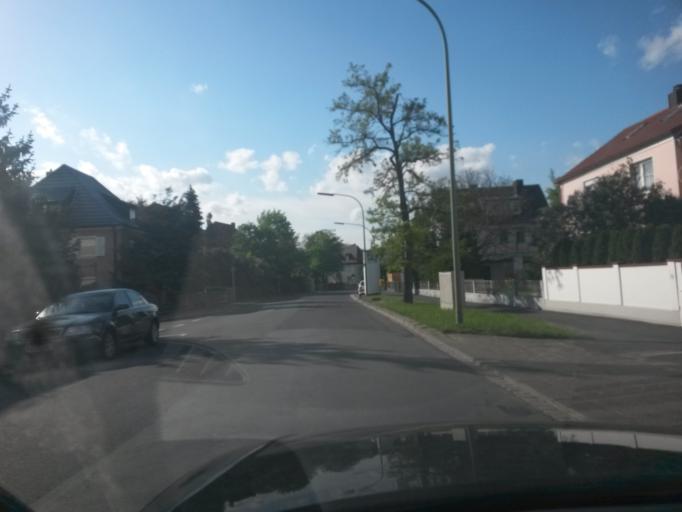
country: DE
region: Bavaria
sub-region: Regierungsbezirk Unterfranken
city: Wuerzburg
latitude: 49.7907
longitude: 9.9587
